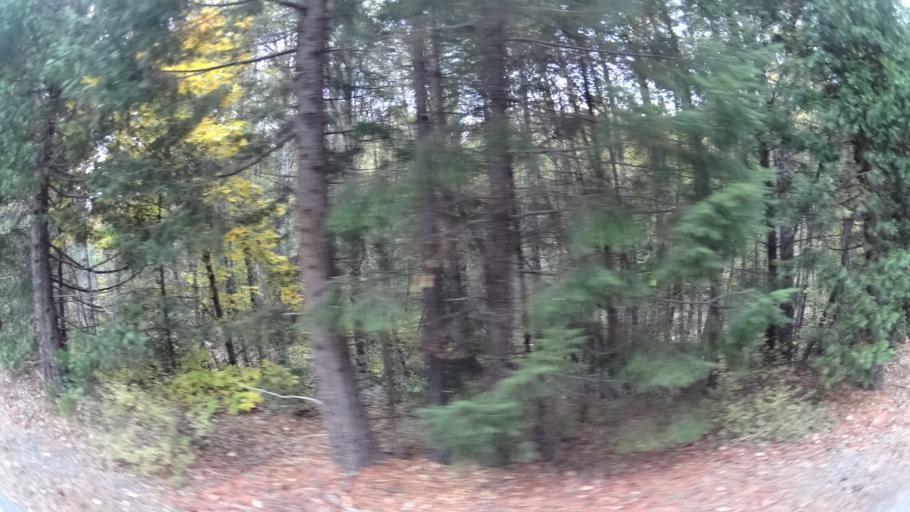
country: US
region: California
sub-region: Siskiyou County
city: Happy Camp
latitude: 41.9166
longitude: -123.4676
